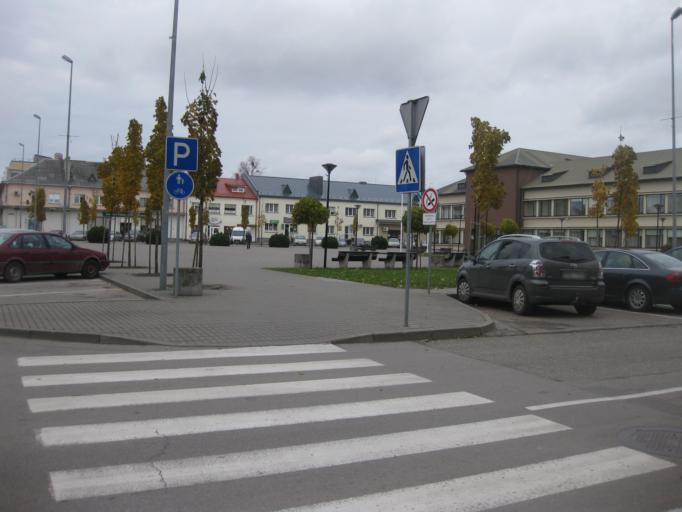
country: LT
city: Prienai
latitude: 54.6350
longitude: 23.9464
